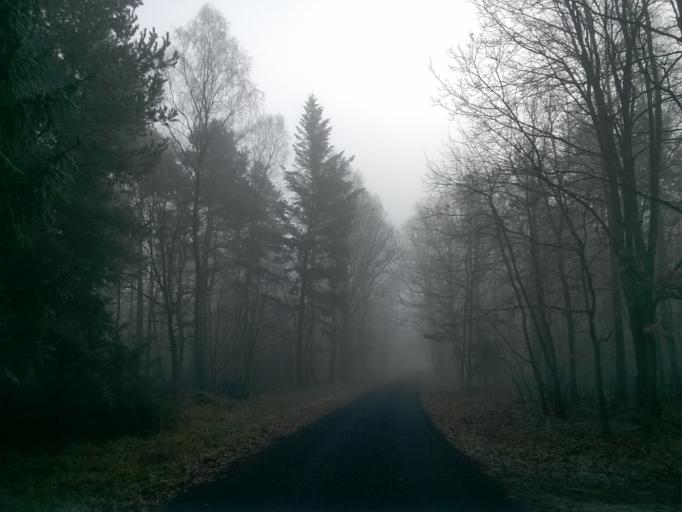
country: PL
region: Kujawsko-Pomorskie
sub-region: Powiat nakielski
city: Kcynia
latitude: 53.0429
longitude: 17.5034
